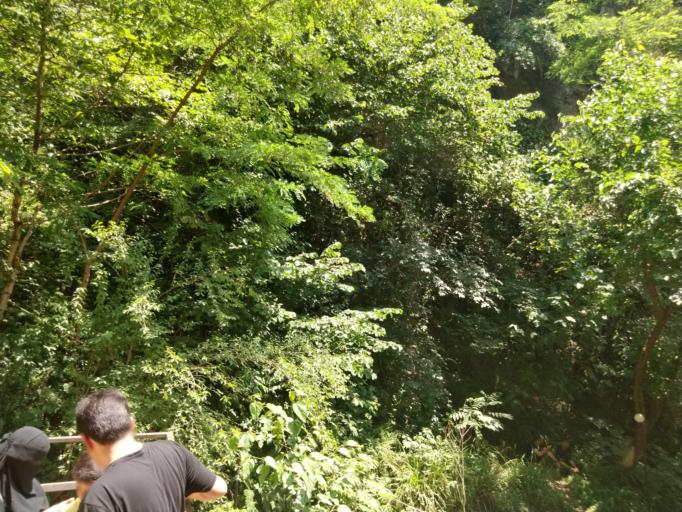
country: GE
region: Ajaria
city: Keda
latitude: 41.5746
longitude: 41.8586
